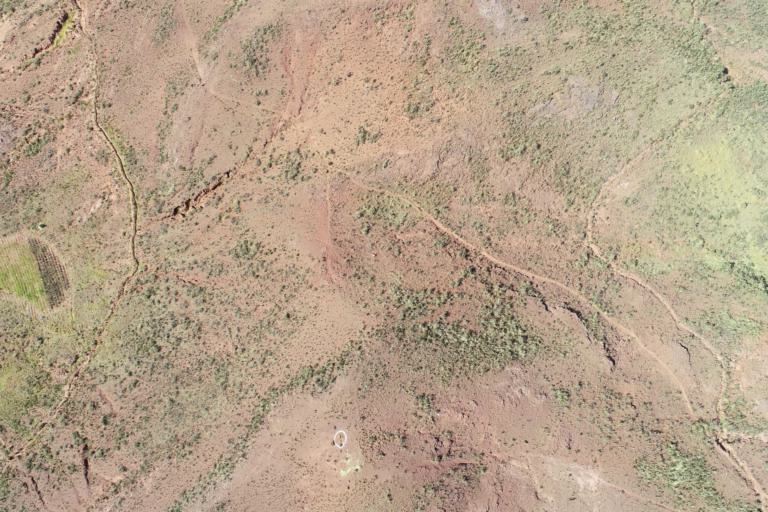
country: BO
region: La Paz
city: Tiahuanaco
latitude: -16.5987
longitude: -68.7613
